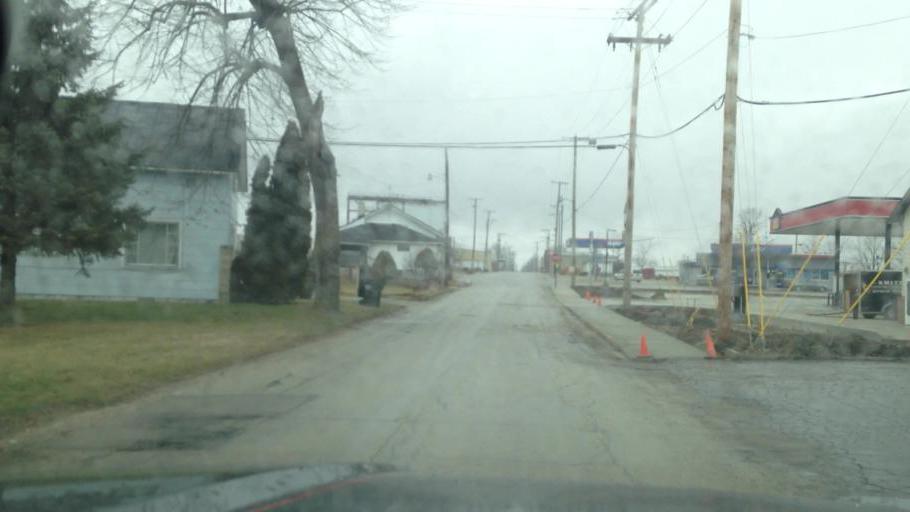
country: US
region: Ohio
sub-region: Darke County
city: Union City
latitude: 40.1965
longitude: -84.8060
